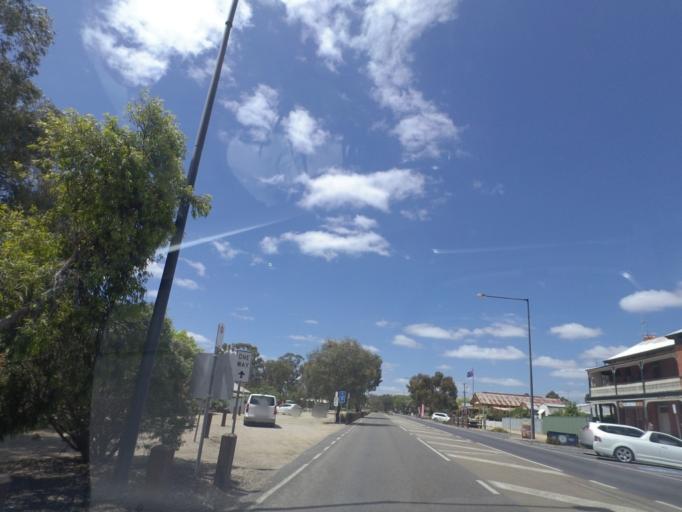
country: AU
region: Victoria
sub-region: Wangaratta
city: Wangaratta
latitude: -36.4637
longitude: 146.2239
